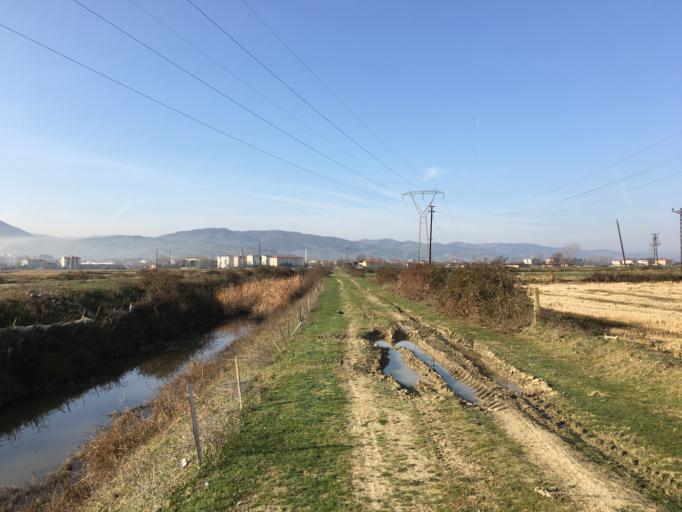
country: TR
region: Samsun
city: Alacam
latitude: 41.6227
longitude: 35.6248
